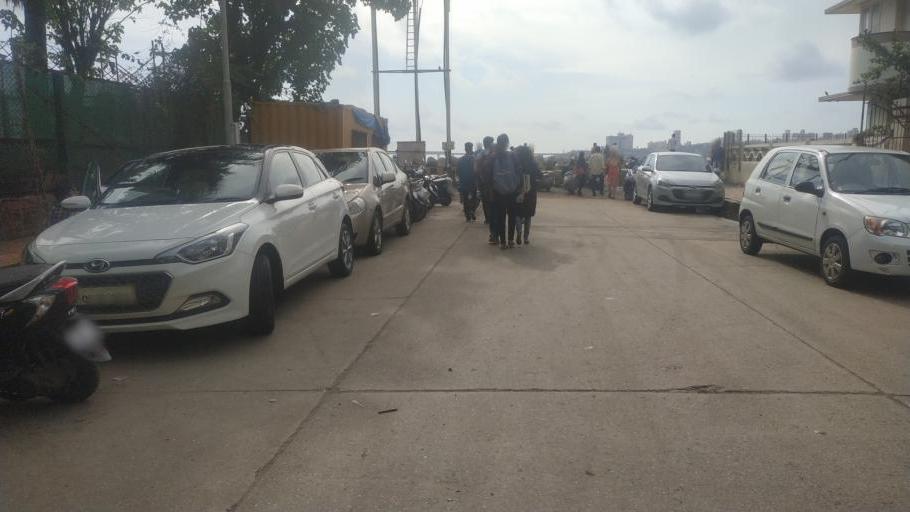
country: IN
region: Maharashtra
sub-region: Mumbai Suburban
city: Mumbai
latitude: 19.0298
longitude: 72.8370
